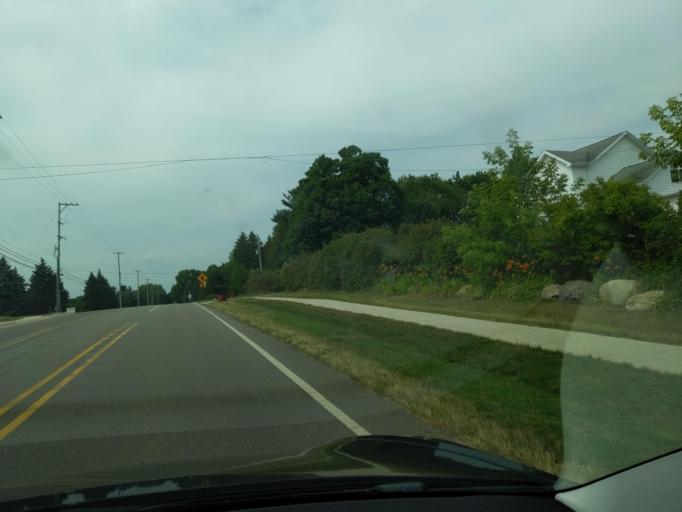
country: US
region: Michigan
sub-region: Clinton County
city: DeWitt
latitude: 42.8271
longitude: -84.6027
